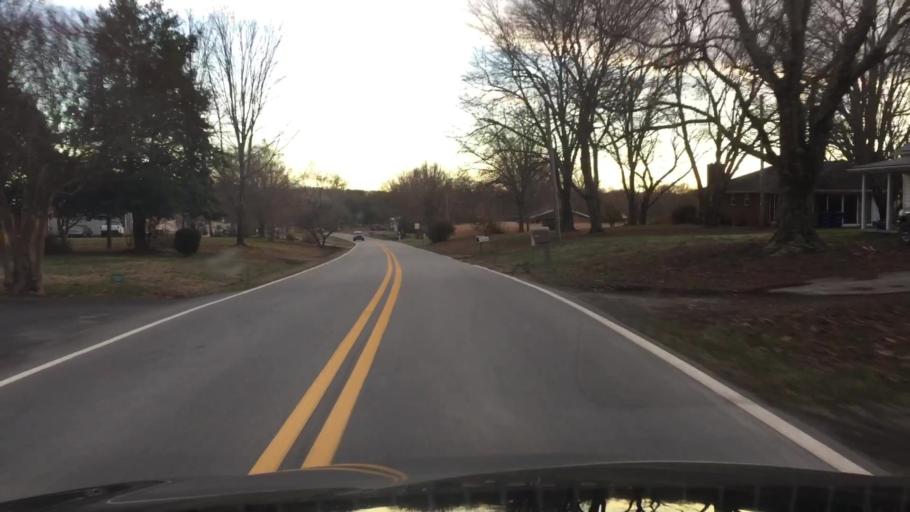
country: US
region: North Carolina
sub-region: Rockingham County
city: Reidsville
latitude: 36.4091
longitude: -79.6577
